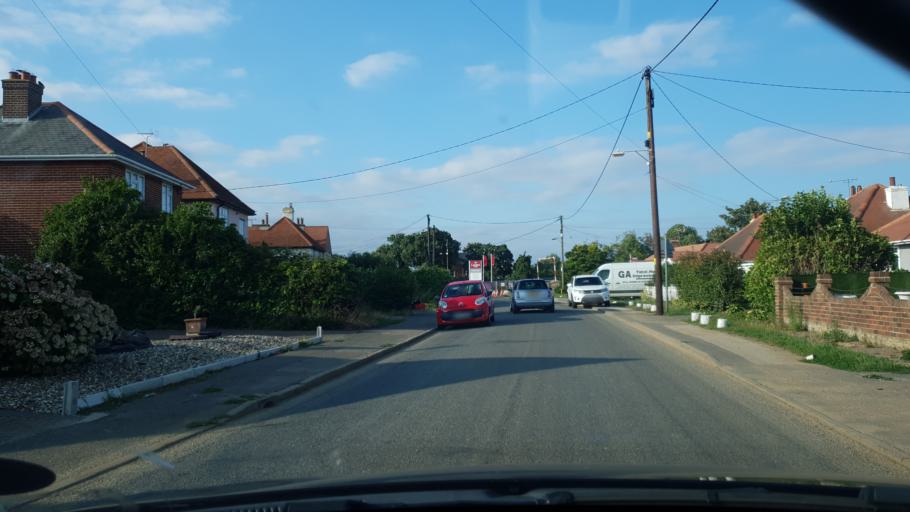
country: GB
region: England
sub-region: Essex
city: Frinton-on-Sea
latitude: 51.8442
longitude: 1.2212
